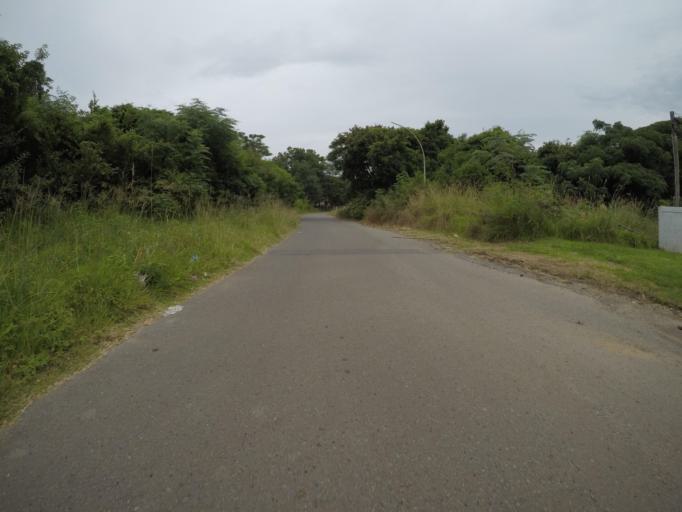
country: ZA
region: Eastern Cape
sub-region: Buffalo City Metropolitan Municipality
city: East London
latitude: -32.9967
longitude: 27.8581
